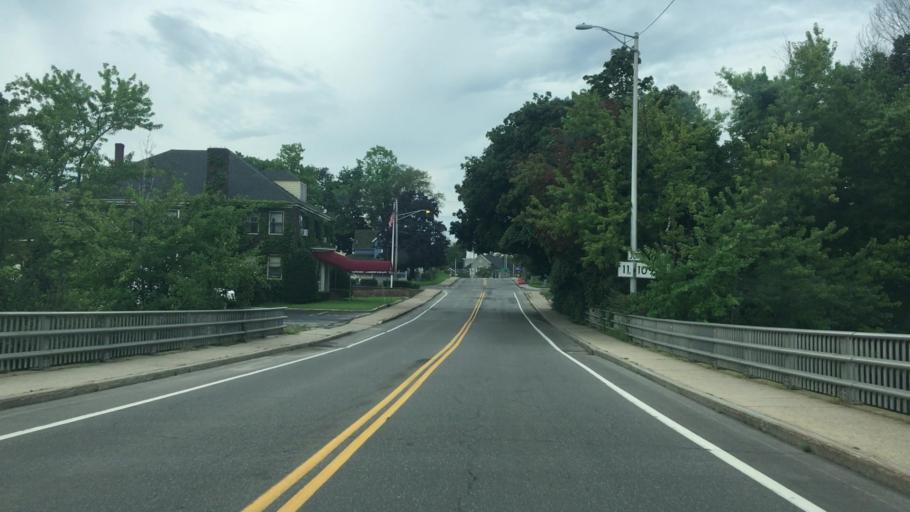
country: US
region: Maine
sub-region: York County
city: Sanford (historical)
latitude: 43.4429
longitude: -70.7757
